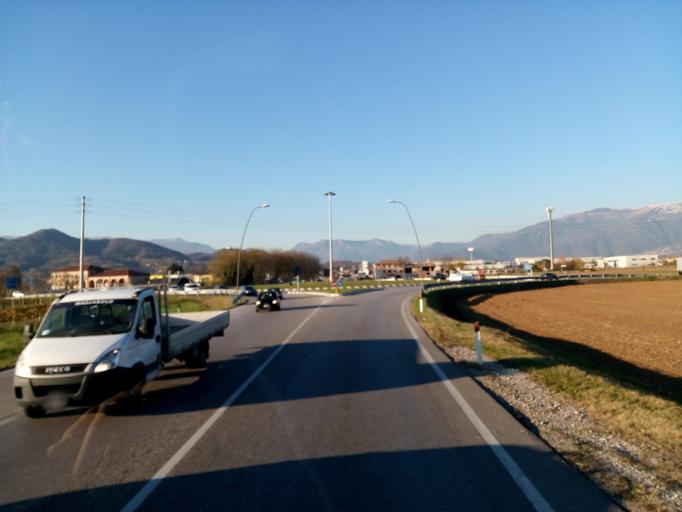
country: IT
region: Veneto
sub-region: Provincia di Treviso
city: Crocetta-Nogare
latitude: 45.8128
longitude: 12.0167
